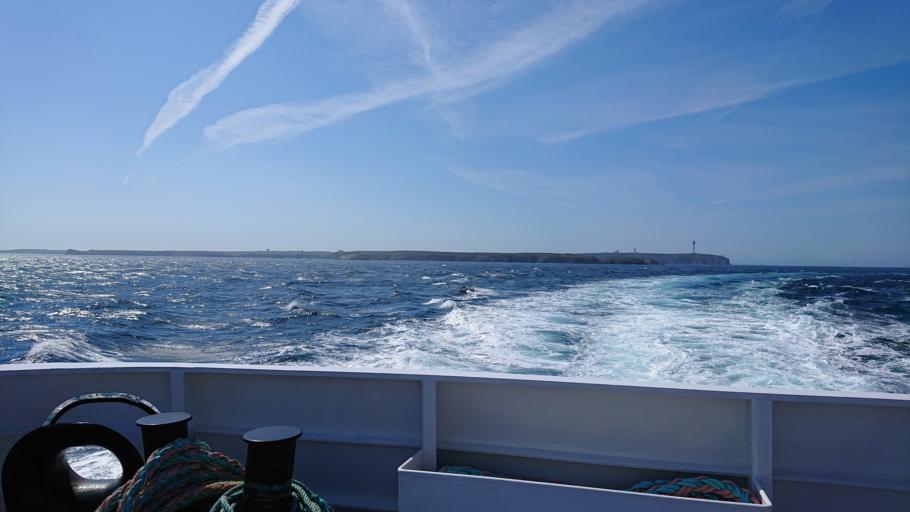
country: FR
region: Brittany
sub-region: Departement du Finistere
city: Porspoder
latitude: 48.4555
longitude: -5.0159
